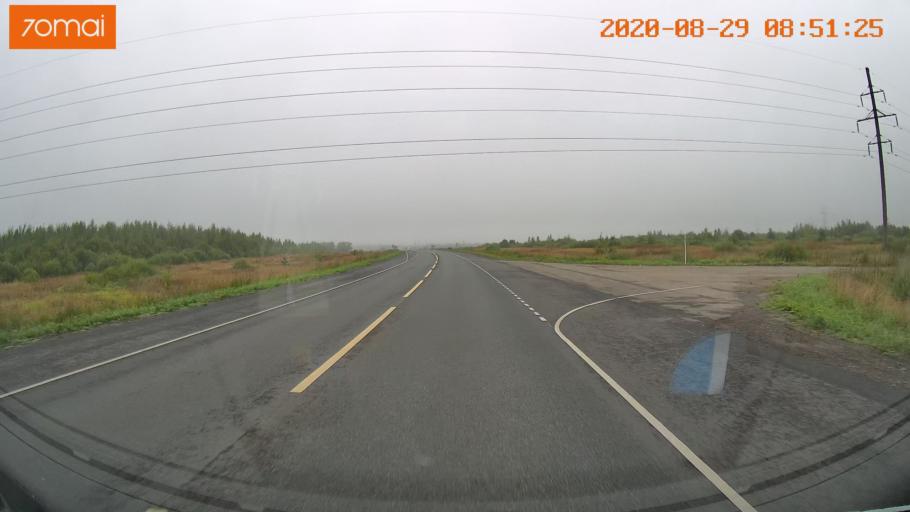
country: RU
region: Ivanovo
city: Vichuga
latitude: 57.1959
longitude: 41.8790
